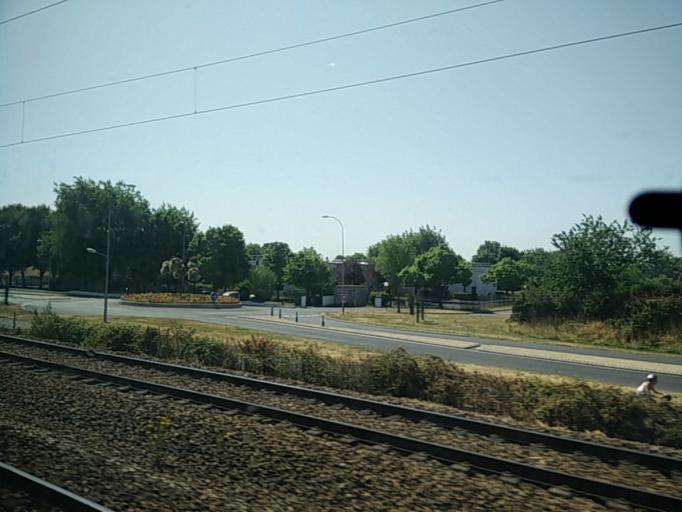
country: FR
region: Ile-de-France
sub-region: Departement de Seine-et-Marne
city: Roissy-en-Brie
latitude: 48.8002
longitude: 2.6367
